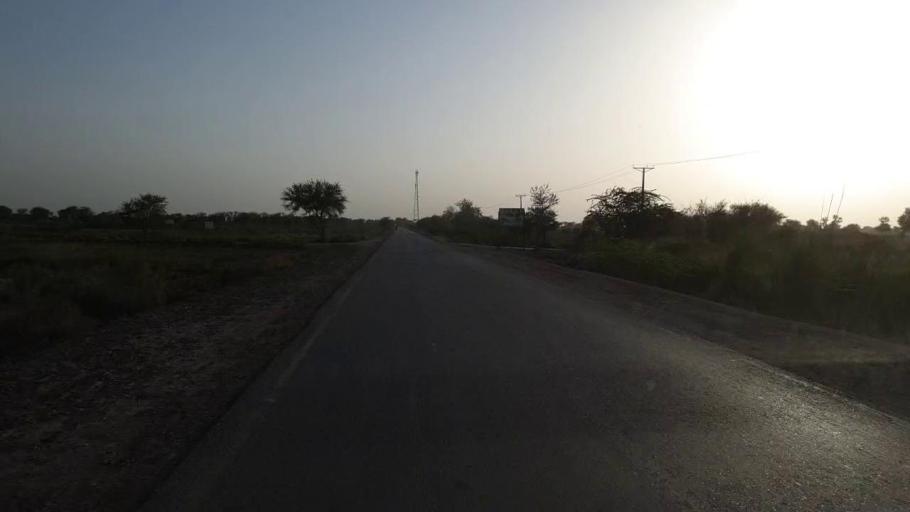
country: PK
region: Sindh
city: Jam Sahib
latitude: 26.2710
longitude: 68.5347
